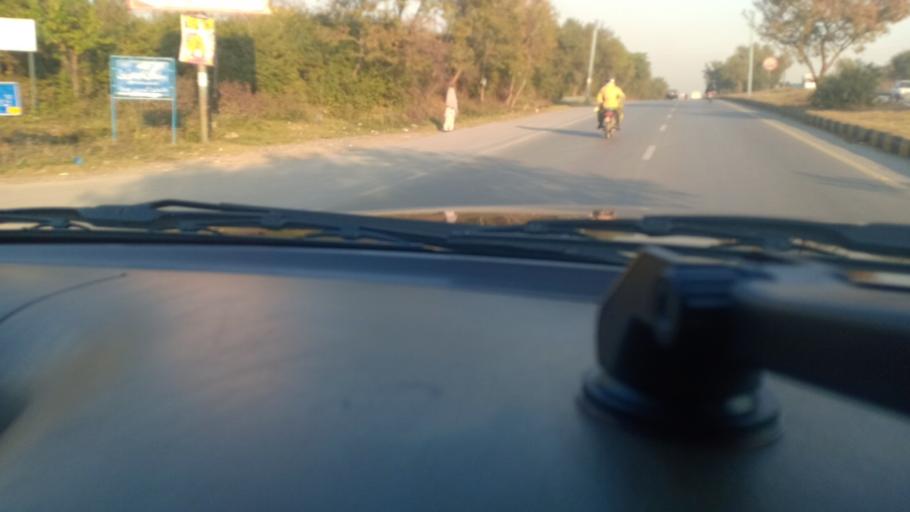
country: PK
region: Islamabad
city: Islamabad
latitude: 33.7348
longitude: 73.1602
